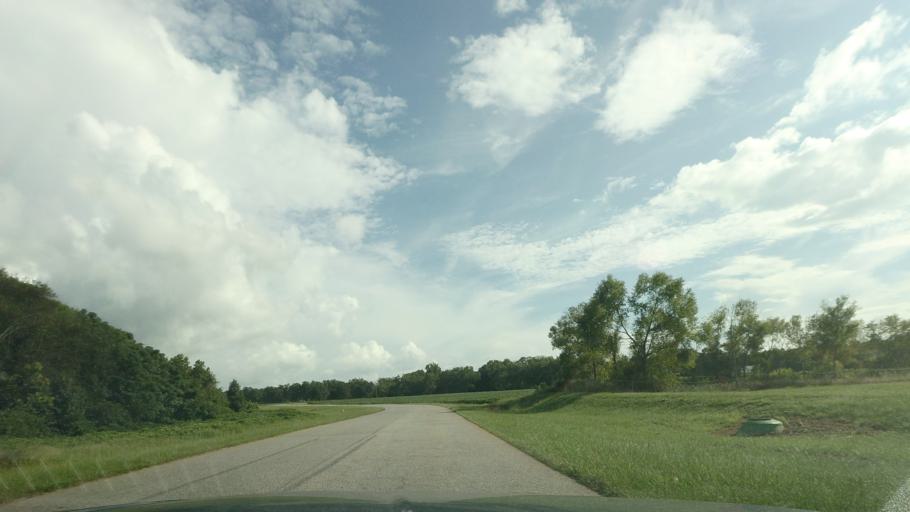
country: US
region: Georgia
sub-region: Peach County
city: Byron
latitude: 32.6439
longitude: -83.7406
